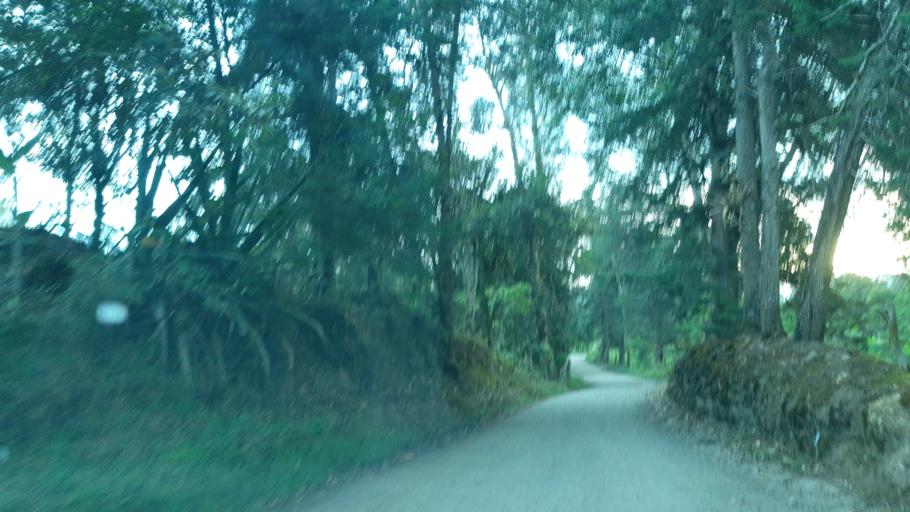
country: CO
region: Boyaca
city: Garagoa
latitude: 5.1051
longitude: -73.3568
